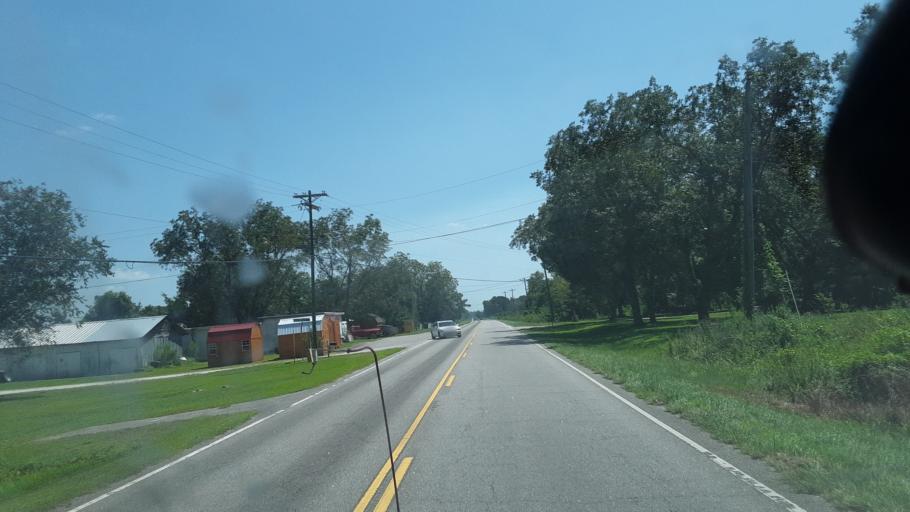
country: US
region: South Carolina
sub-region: Horry County
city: North Myrtle Beach
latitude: 33.8608
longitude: -78.7260
